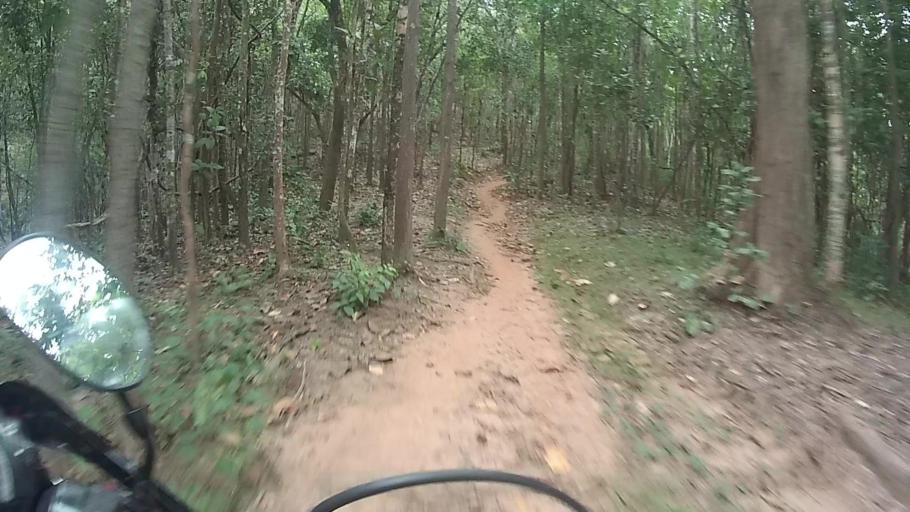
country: TH
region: Chiang Mai
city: Mae On
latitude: 18.7632
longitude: 99.3155
